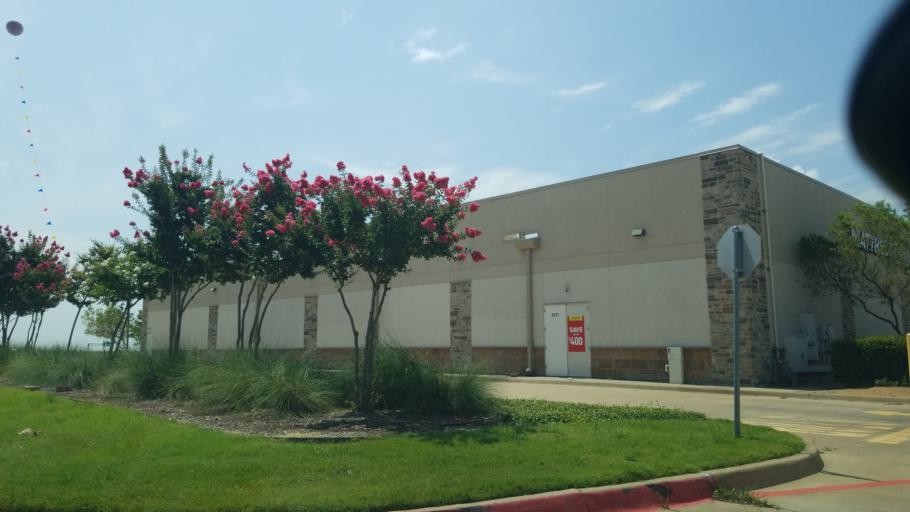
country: US
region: Texas
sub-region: Dallas County
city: Coppell
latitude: 32.9220
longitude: -96.9809
